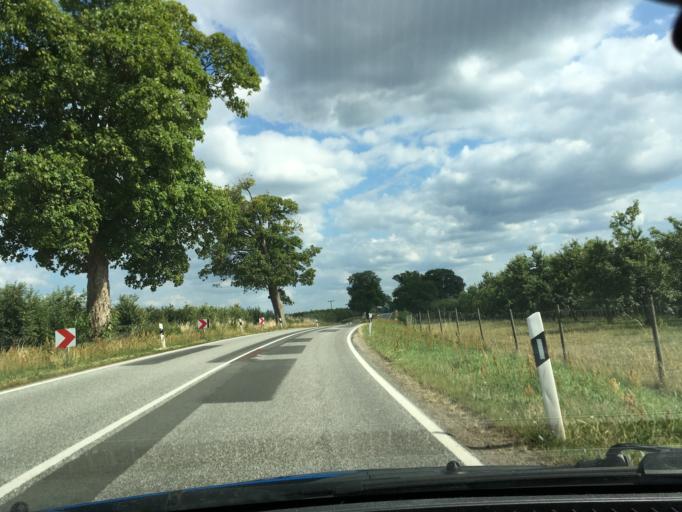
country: DE
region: Mecklenburg-Vorpommern
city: Lubtheen
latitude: 53.3858
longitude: 11.0691
